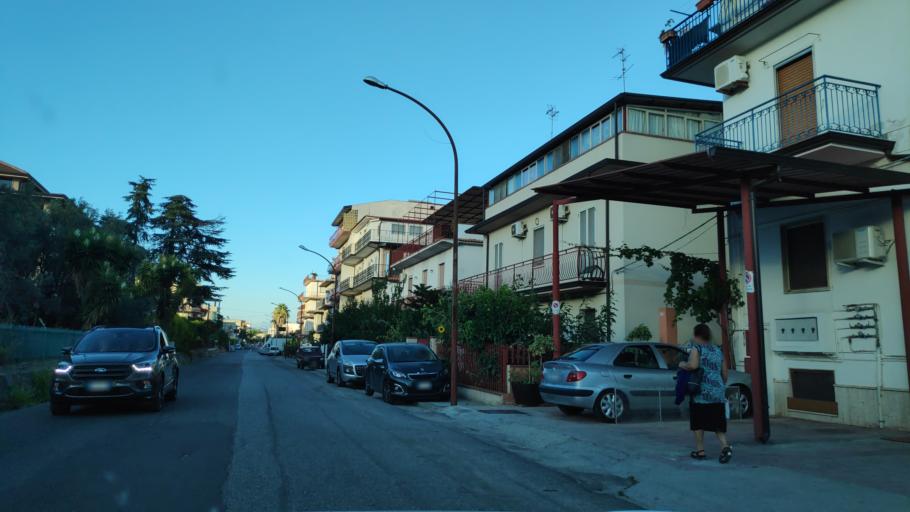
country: IT
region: Calabria
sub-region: Provincia di Reggio Calabria
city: Locri
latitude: 38.2361
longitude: 16.2488
